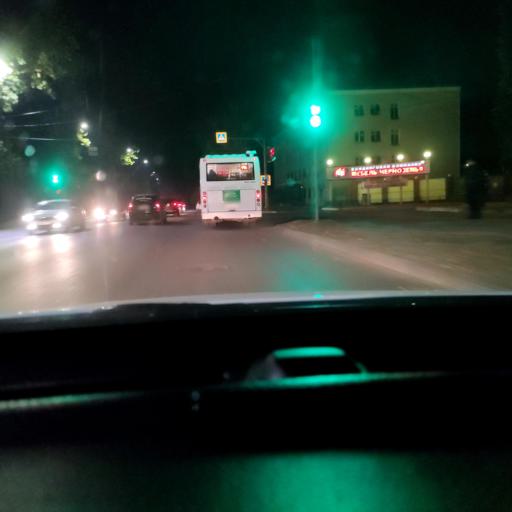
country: RU
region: Voronezj
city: Somovo
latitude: 51.7174
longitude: 39.2743
